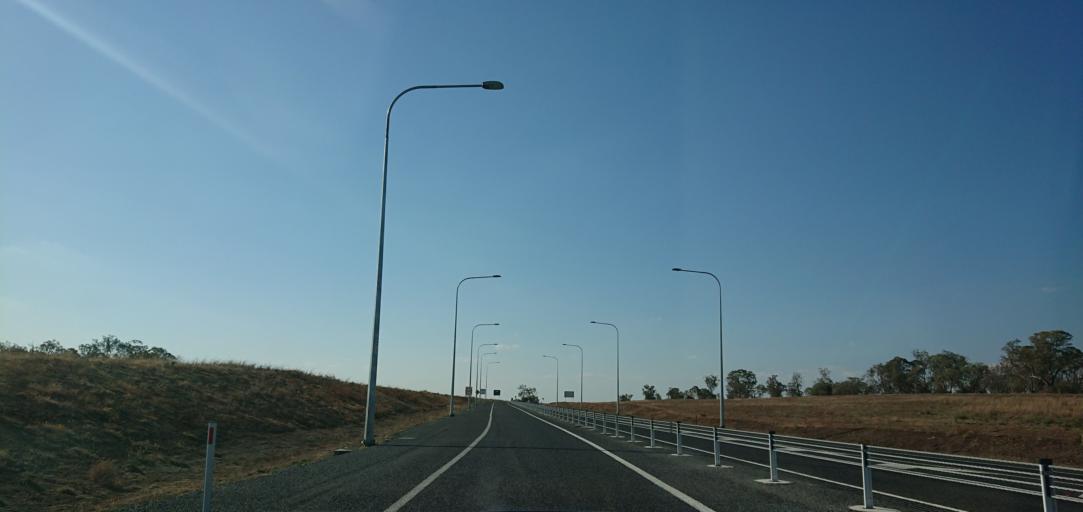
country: AU
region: Queensland
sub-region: Toowoomba
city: Westbrook
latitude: -27.6101
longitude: 151.7866
